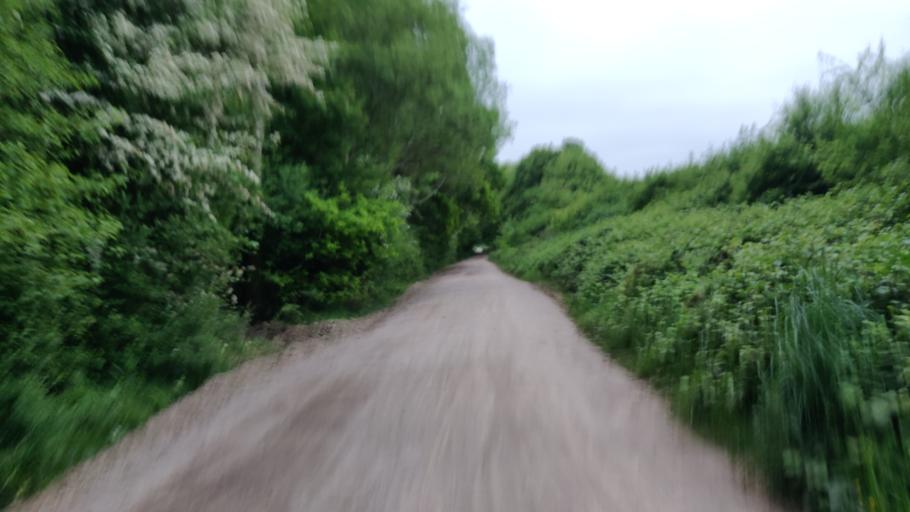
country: GB
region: England
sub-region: West Sussex
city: Partridge Green
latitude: 50.9854
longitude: -0.3148
